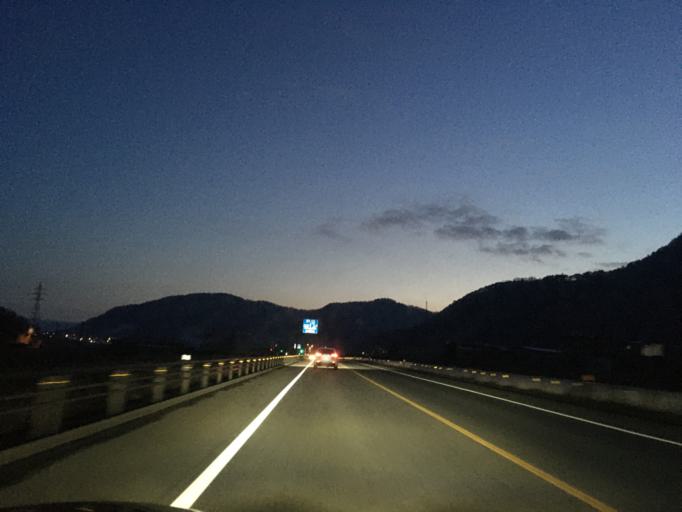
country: JP
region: Yamagata
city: Takahata
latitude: 38.0935
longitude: 140.1948
